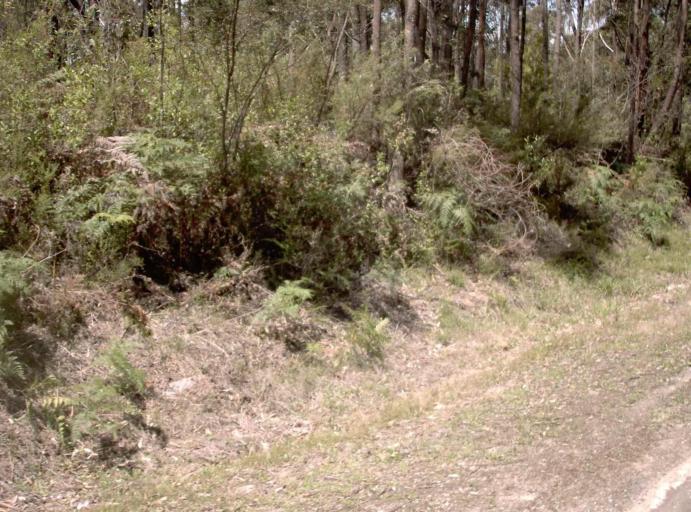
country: AU
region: Victoria
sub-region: East Gippsland
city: Lakes Entrance
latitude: -37.7001
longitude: 148.6413
